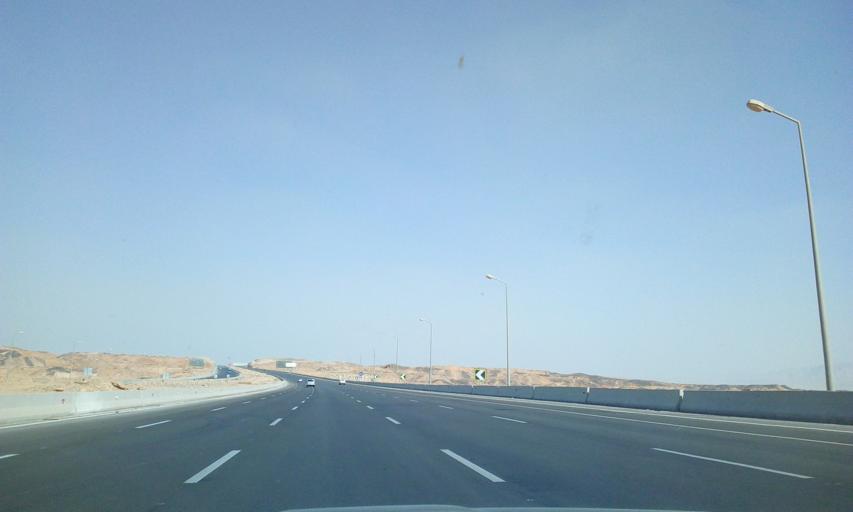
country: EG
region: As Suways
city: Ain Sukhna
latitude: 29.6946
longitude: 32.1150
